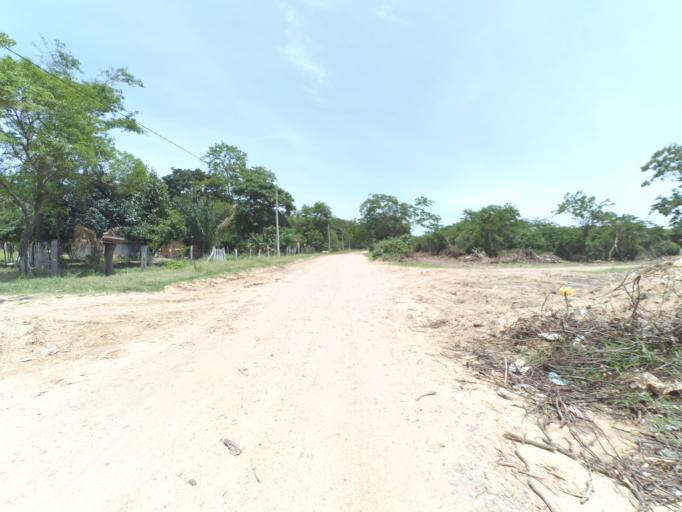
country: BO
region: Santa Cruz
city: Santa Cruz de la Sierra
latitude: -17.8208
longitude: -63.2536
